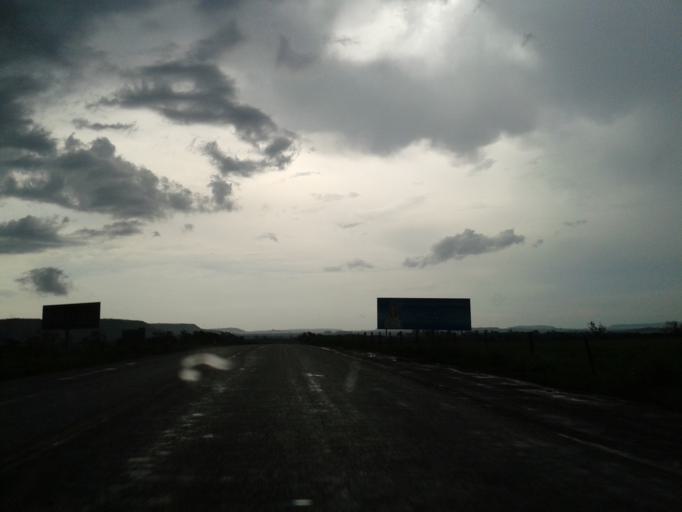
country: BR
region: Goias
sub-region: Quirinopolis
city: Quirinopolis
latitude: -18.4367
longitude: -50.4180
